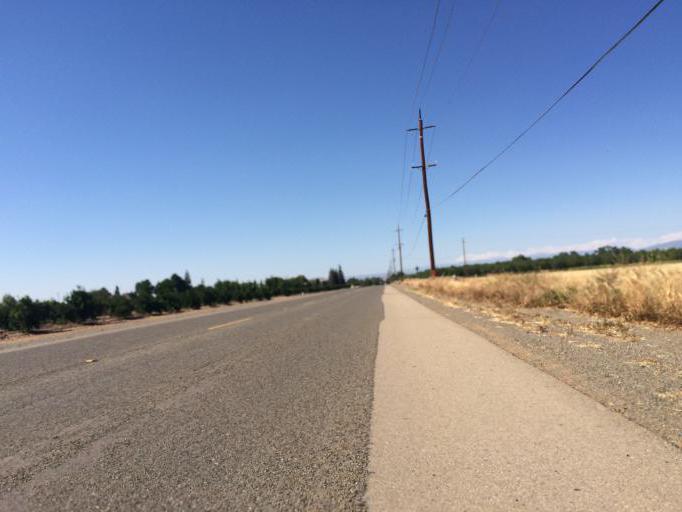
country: US
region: California
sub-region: Fresno County
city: Sanger
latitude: 36.7742
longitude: -119.6101
